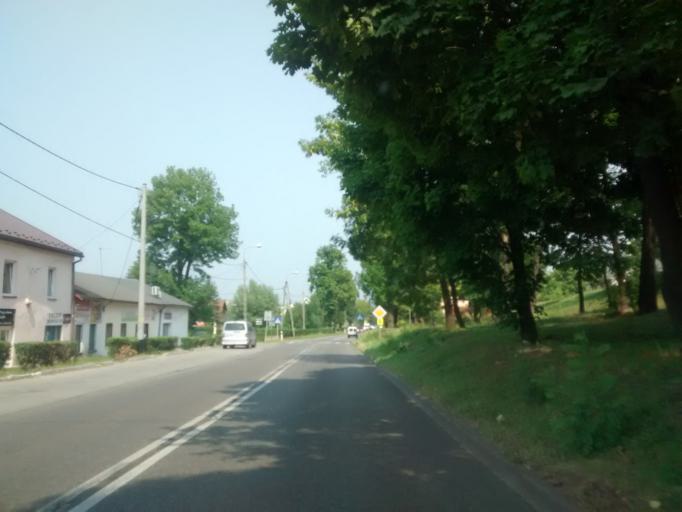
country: PL
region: Lesser Poland Voivodeship
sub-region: Powiat olkuski
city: Klucze
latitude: 50.3379
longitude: 19.5621
